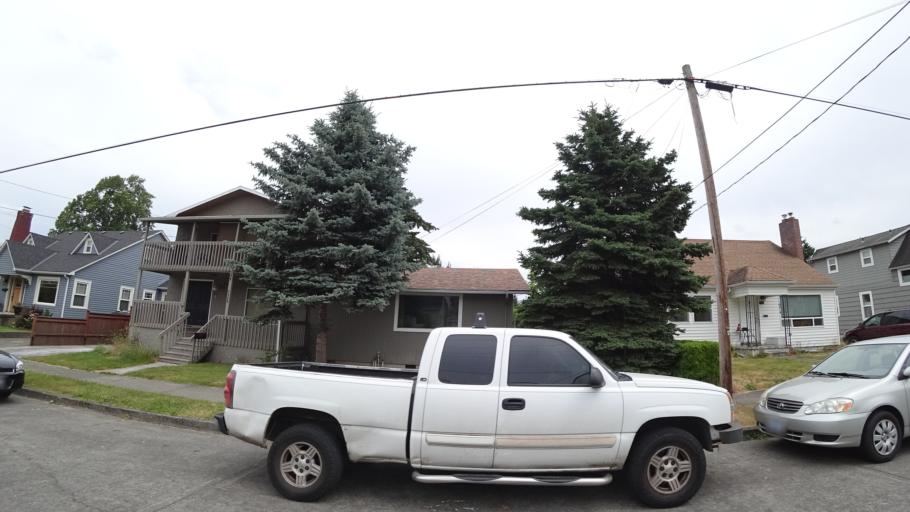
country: US
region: Oregon
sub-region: Multnomah County
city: Portland
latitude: 45.5762
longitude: -122.6925
